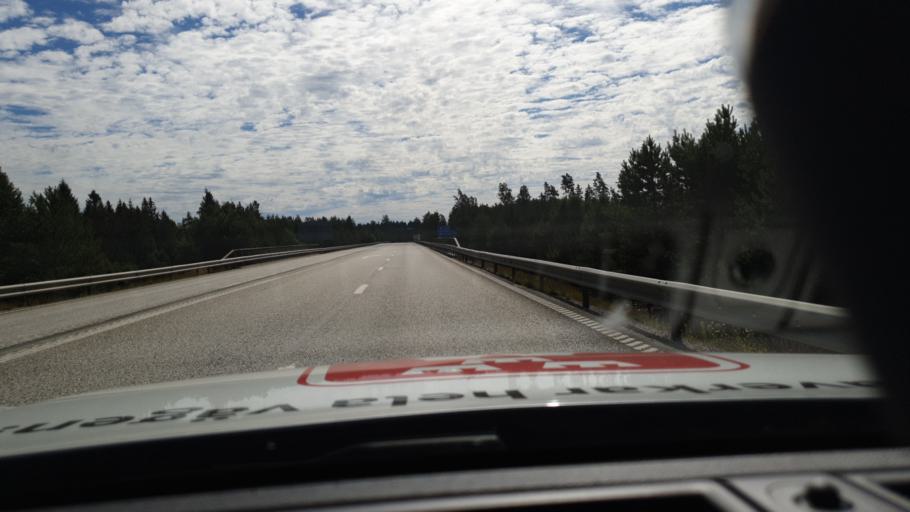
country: SE
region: Joenkoeping
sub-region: Jonkopings Kommun
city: Odensjo
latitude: 57.6186
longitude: 14.1973
